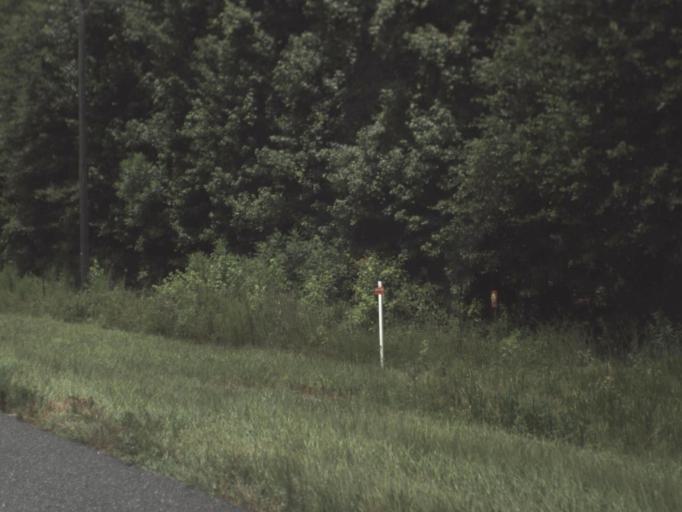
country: US
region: Florida
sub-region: Taylor County
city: Perry
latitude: 30.2967
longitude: -83.7420
